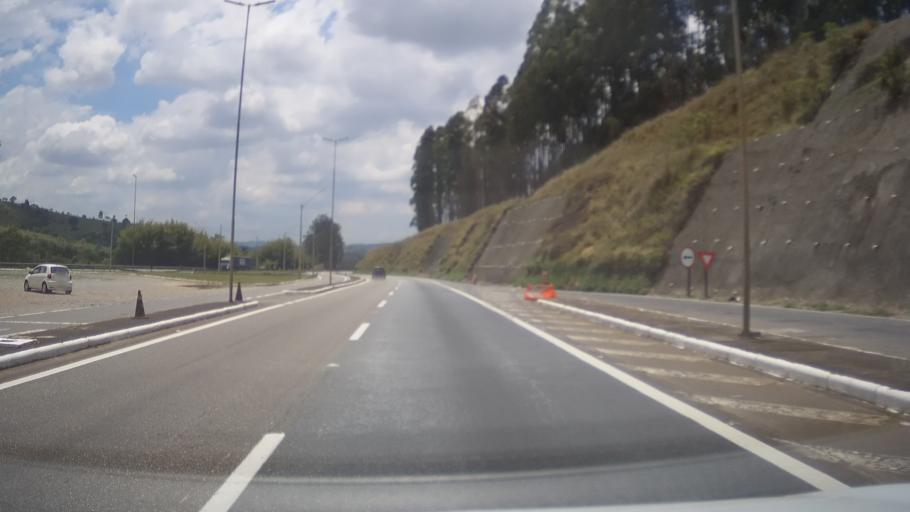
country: BR
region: Minas Gerais
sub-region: Tres Coracoes
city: Tres Coracoes
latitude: -21.6904
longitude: -45.3493
